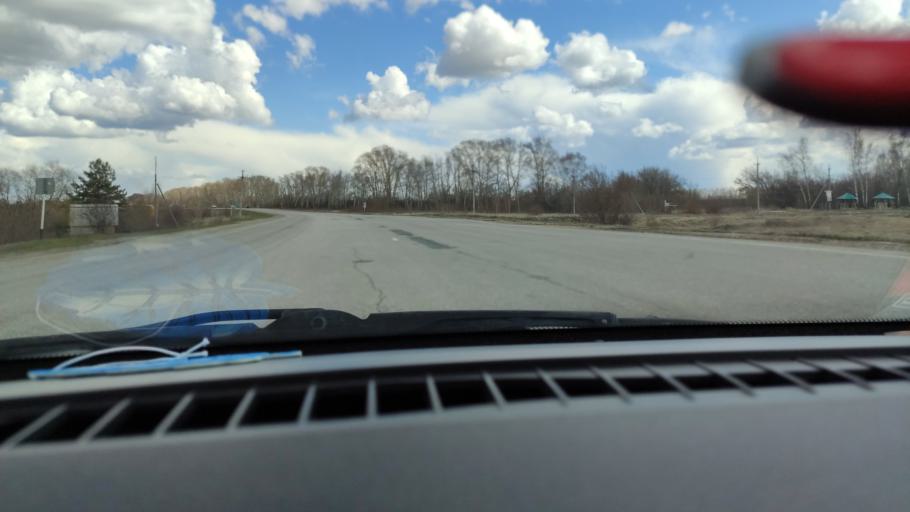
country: RU
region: Samara
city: Varlamovo
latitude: 53.1228
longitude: 48.3032
